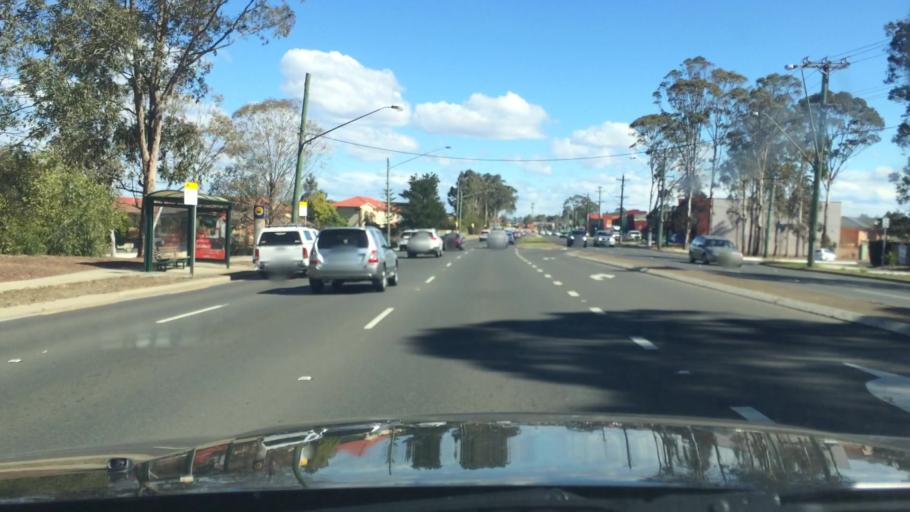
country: AU
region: New South Wales
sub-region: Campbelltown Municipality
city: Glenfield
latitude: -33.9535
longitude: 150.8997
